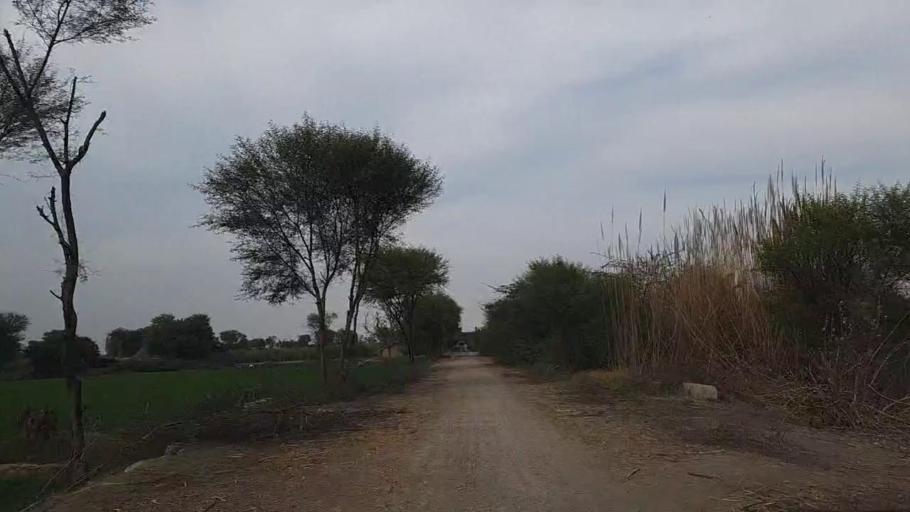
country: PK
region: Sindh
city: Daur
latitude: 26.5185
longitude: 68.4162
